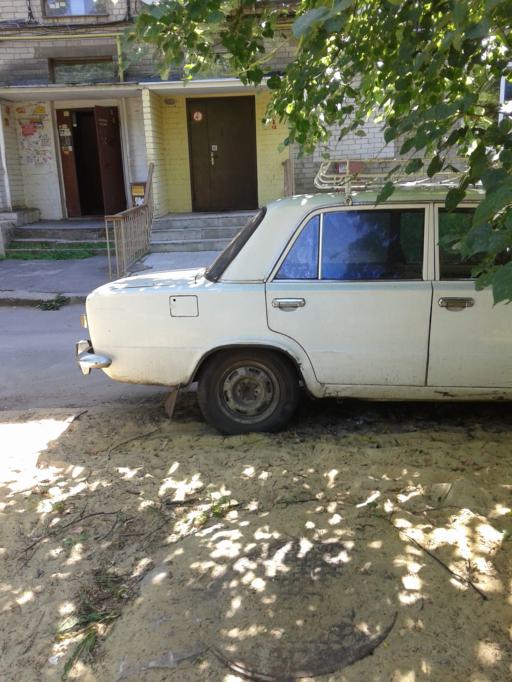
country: RU
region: Voronezj
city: Voronezh
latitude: 51.6538
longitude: 39.1429
